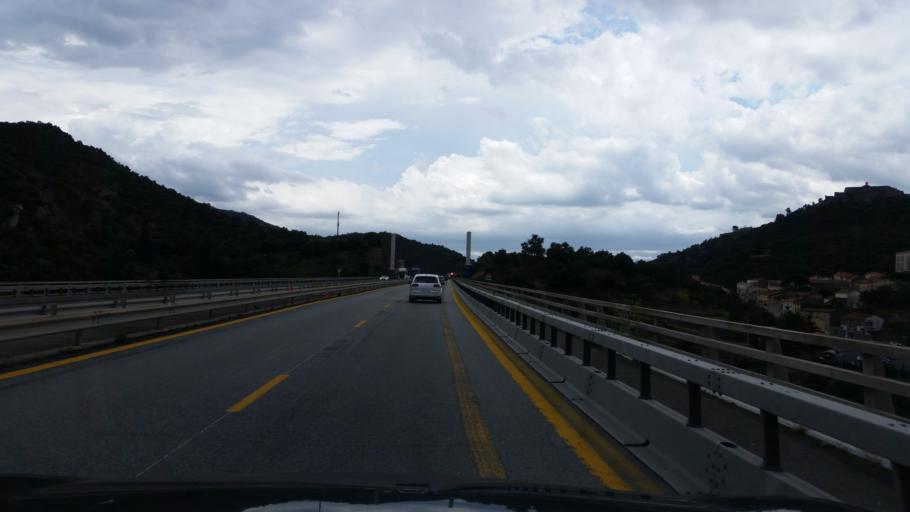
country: FR
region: Languedoc-Roussillon
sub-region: Departement des Pyrenees-Orientales
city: Montesquiu d'Albera
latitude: 42.4692
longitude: 2.8643
